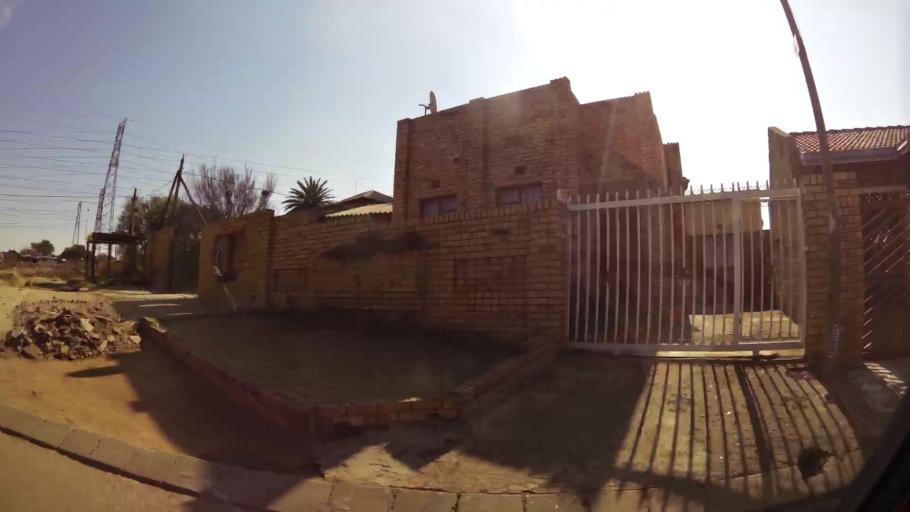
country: ZA
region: Gauteng
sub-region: City of Johannesburg Metropolitan Municipality
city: Soweto
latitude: -26.2498
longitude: 27.9349
